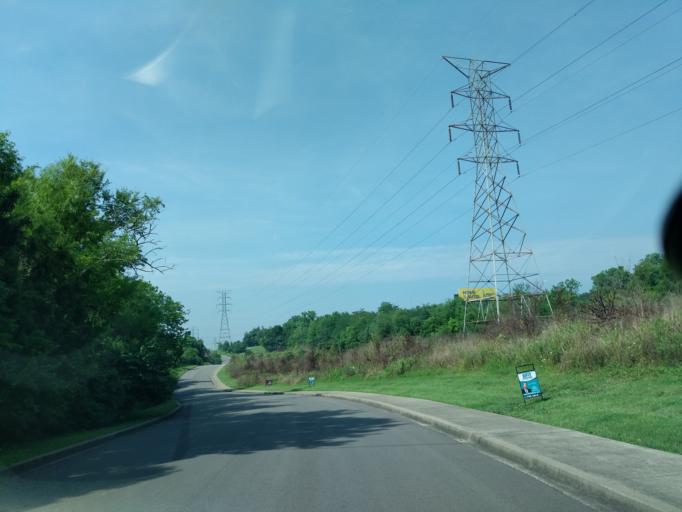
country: US
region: Tennessee
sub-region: Davidson County
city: Goodlettsville
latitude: 36.2999
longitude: -86.7099
